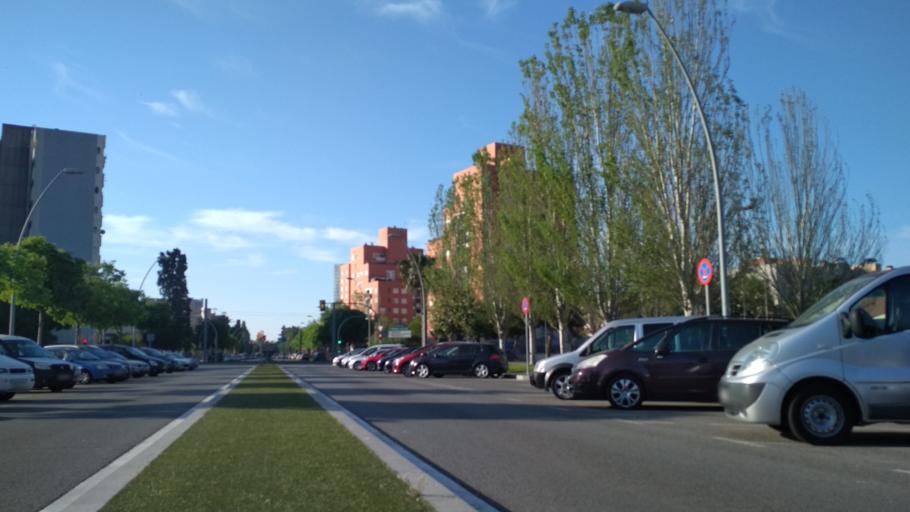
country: ES
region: Catalonia
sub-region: Provincia de Barcelona
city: Sant Adria de Besos
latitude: 41.4198
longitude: 2.2164
